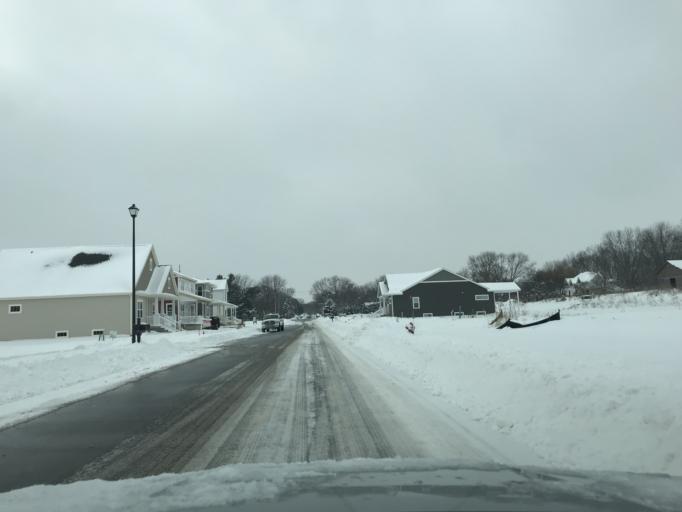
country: US
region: Wisconsin
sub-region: Dane County
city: Sun Prairie
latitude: 43.1677
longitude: -89.2828
